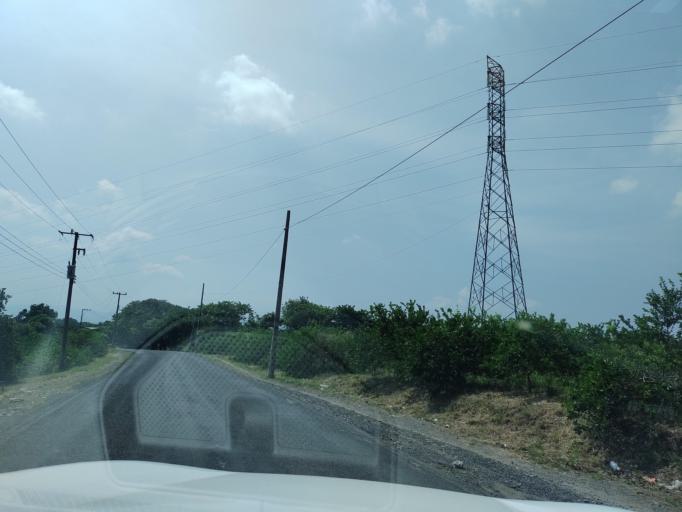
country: MX
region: Veracruz
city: Martinez de la Torre
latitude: 20.0893
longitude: -97.0538
